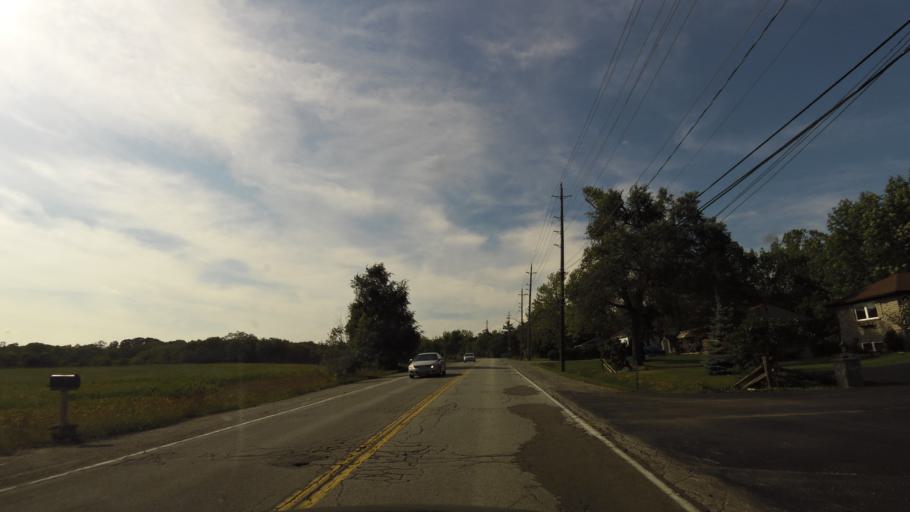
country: CA
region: Ontario
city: Hamilton
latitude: 43.3201
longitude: -79.8712
